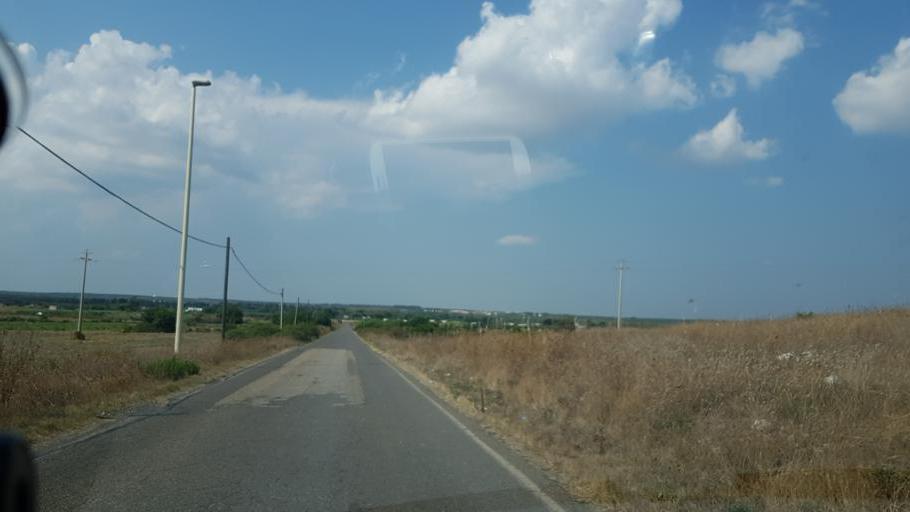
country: IT
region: Apulia
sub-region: Provincia di Taranto
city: Maruggio
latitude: 40.3052
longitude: 17.6345
